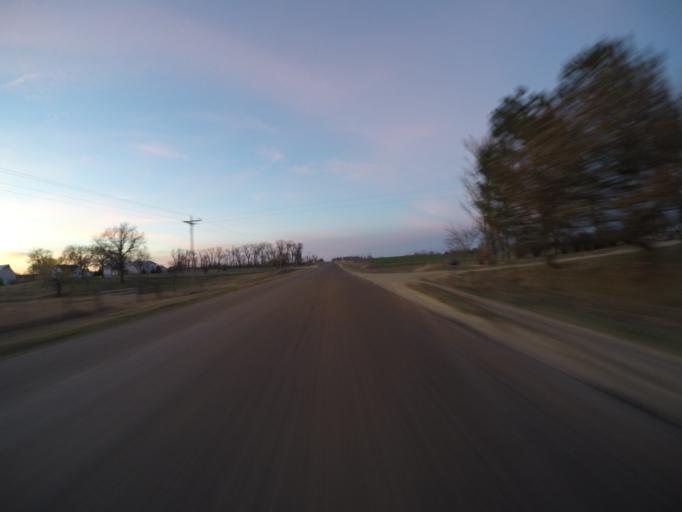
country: US
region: Kansas
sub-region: Washington County
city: Washington
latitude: 39.7723
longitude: -96.9752
